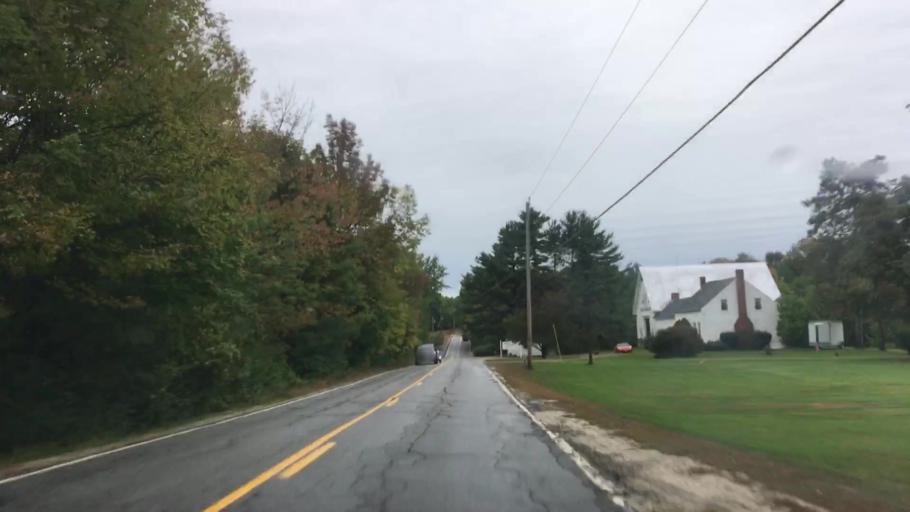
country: US
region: Maine
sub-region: Cumberland County
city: Raymond
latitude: 43.9709
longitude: -70.4682
